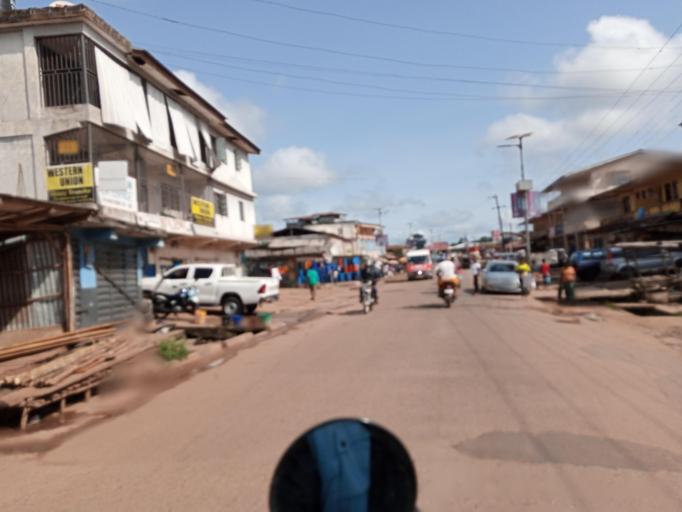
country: SL
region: Southern Province
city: Bo
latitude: 7.9650
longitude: -11.7357
